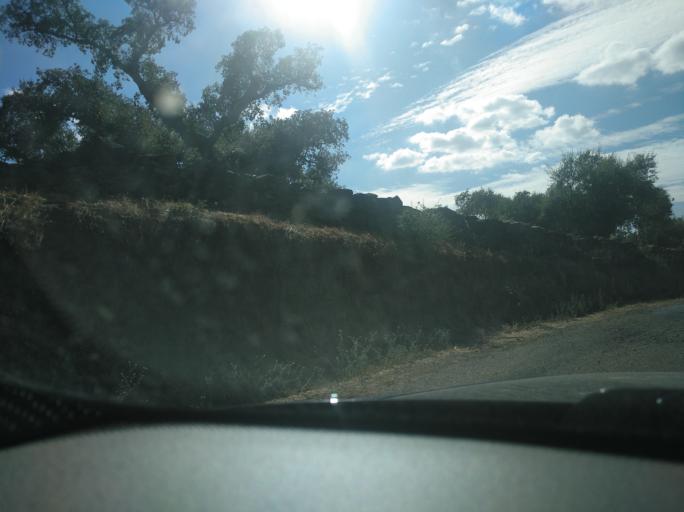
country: ES
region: Extremadura
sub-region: Provincia de Badajoz
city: La Codosera
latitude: 39.1550
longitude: -7.1705
